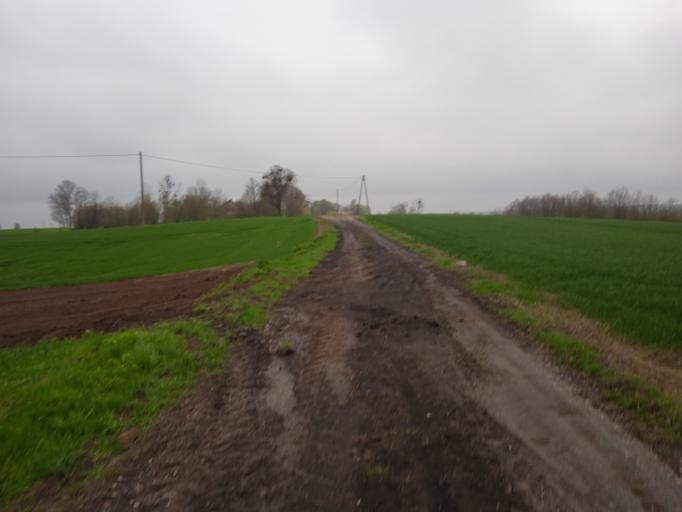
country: PL
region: Kujawsko-Pomorskie
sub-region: Powiat grudziadzki
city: Lasin
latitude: 53.5723
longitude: 19.0562
